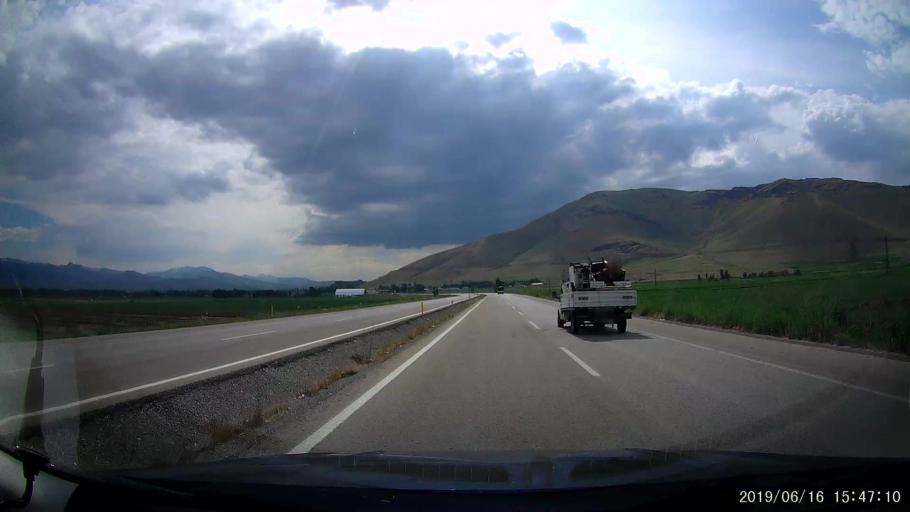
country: TR
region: Erzurum
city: Pasinler
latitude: 39.9889
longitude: 41.7273
